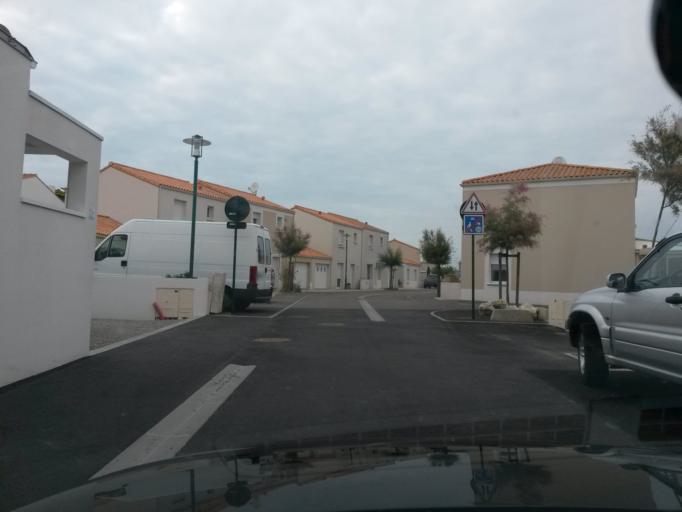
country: FR
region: Pays de la Loire
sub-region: Departement de la Vendee
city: Les Sables-d'Olonne
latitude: 46.4905
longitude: -1.7974
